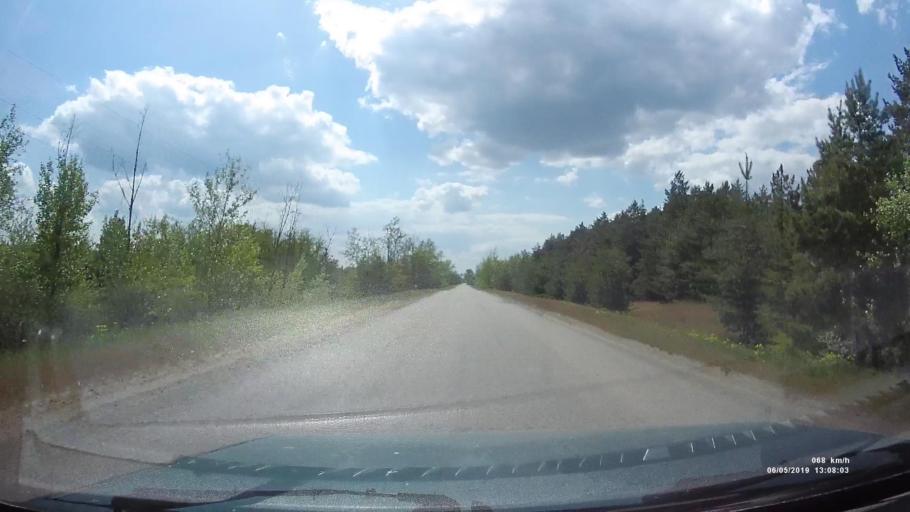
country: RU
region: Rostov
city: Ust'-Donetskiy
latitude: 47.7783
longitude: 40.9996
